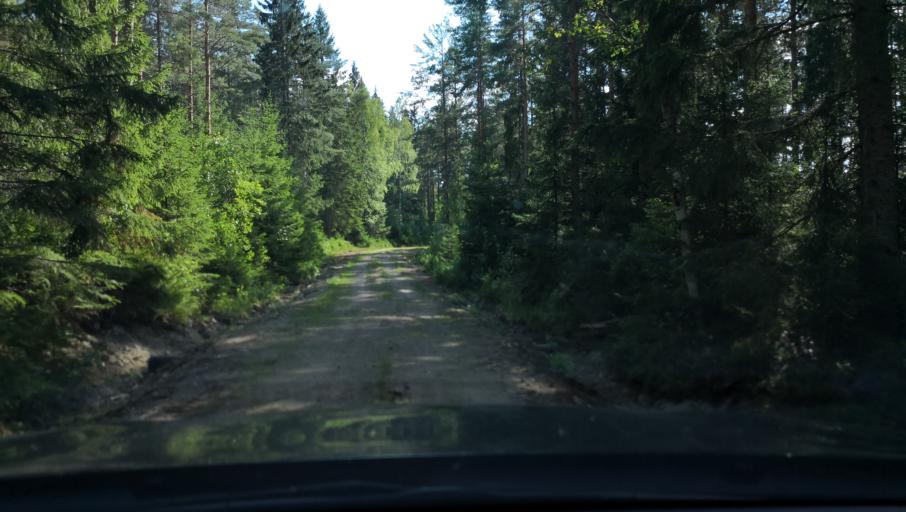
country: SE
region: Vaestmanland
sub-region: Surahammars Kommun
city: Surahammar
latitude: 59.7230
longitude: 16.3111
